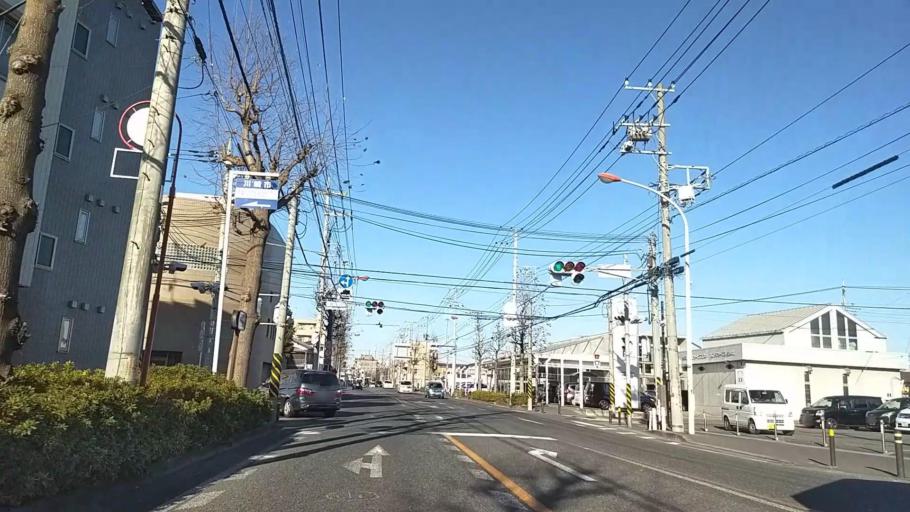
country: JP
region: Tokyo
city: Chofugaoka
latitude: 35.6284
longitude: 139.5399
